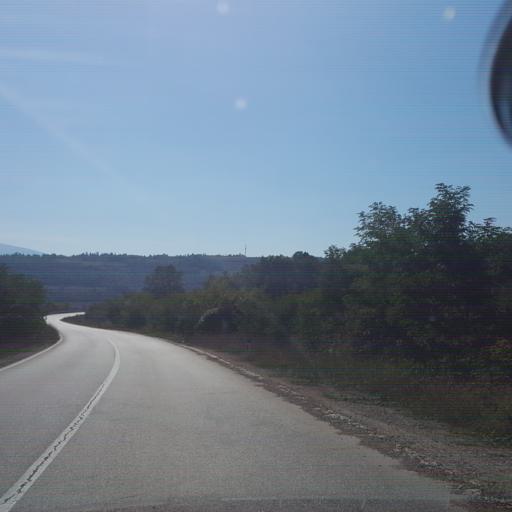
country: RS
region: Central Serbia
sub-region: Nisavski Okrug
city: Svrljig
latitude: 43.4571
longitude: 22.2042
